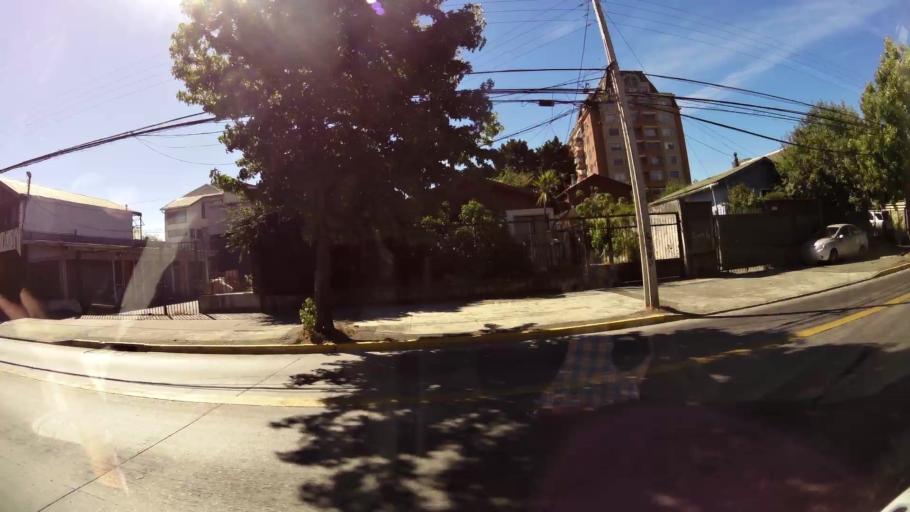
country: CL
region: Biobio
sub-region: Provincia de Concepcion
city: Concepcion
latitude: -36.8163
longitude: -73.0351
